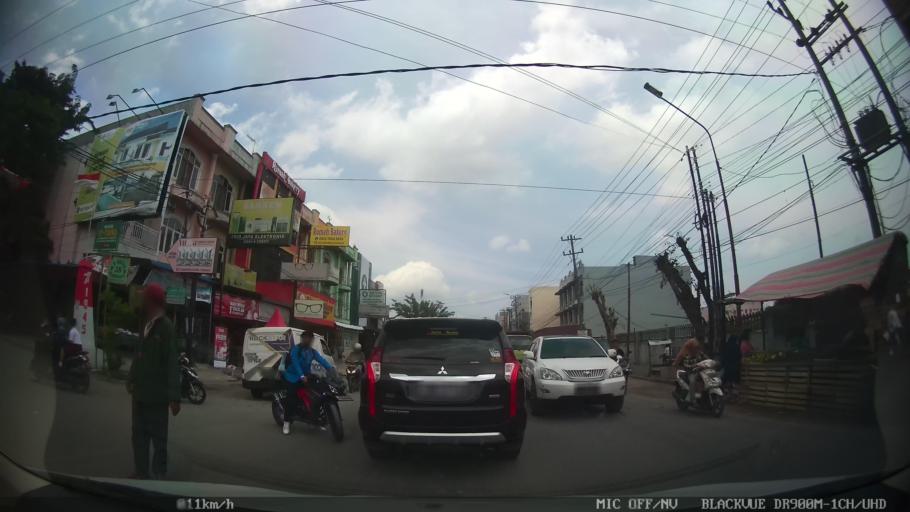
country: ID
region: North Sumatra
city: Labuhan Deli
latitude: 3.6914
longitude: 98.6561
